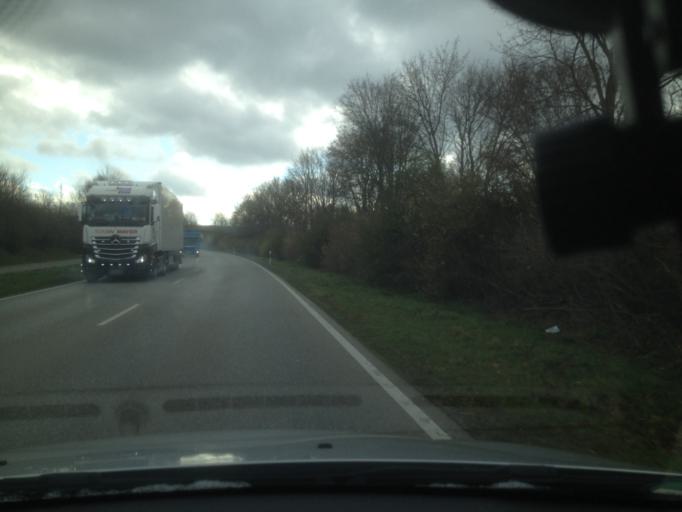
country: DE
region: Bavaria
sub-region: Swabia
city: Mering
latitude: 48.2621
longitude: 10.9699
